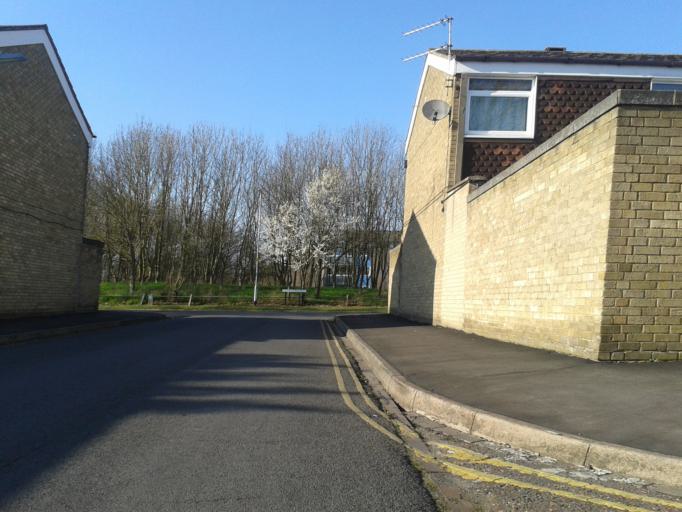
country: GB
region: England
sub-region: Cambridgeshire
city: Cambridge
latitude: 52.2286
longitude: 0.1316
